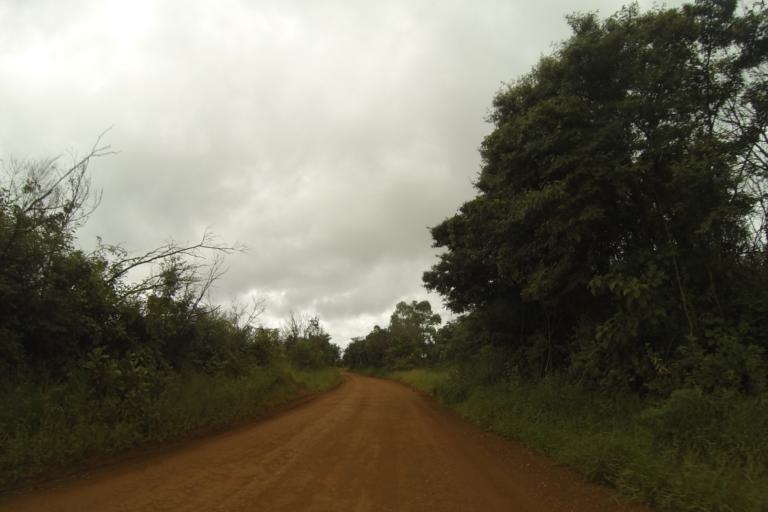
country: BR
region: Minas Gerais
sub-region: Campos Altos
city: Campos Altos
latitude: -19.8314
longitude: -46.3224
